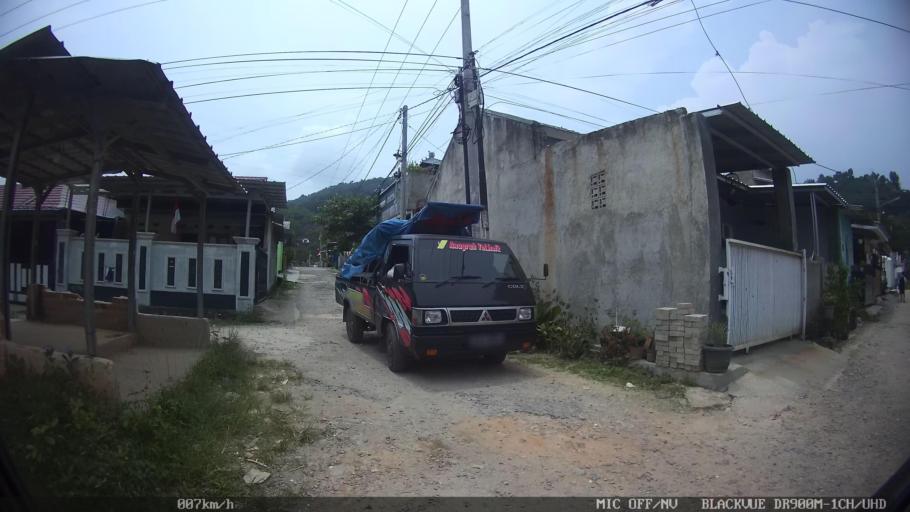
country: ID
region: Lampung
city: Kedaton
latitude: -5.4028
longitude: 105.3262
